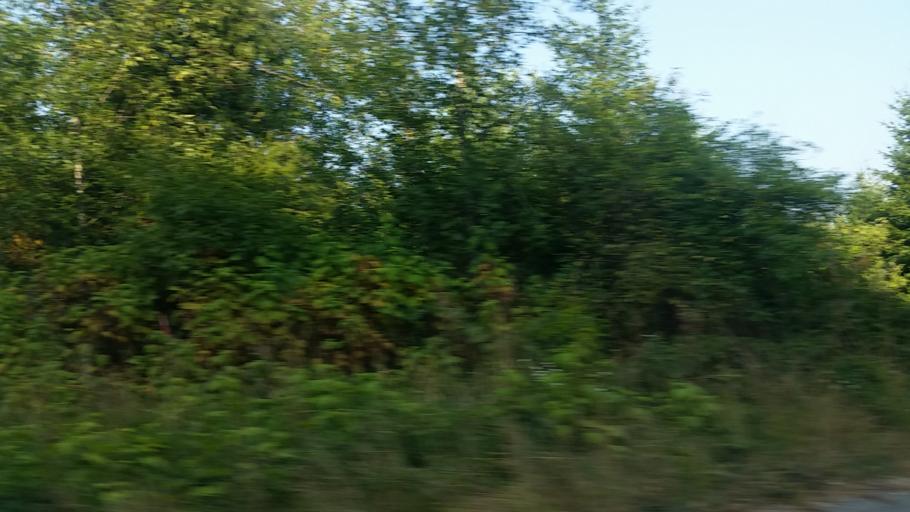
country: US
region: Washington
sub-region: Clallam County
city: Forks
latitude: 47.9431
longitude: -124.4627
